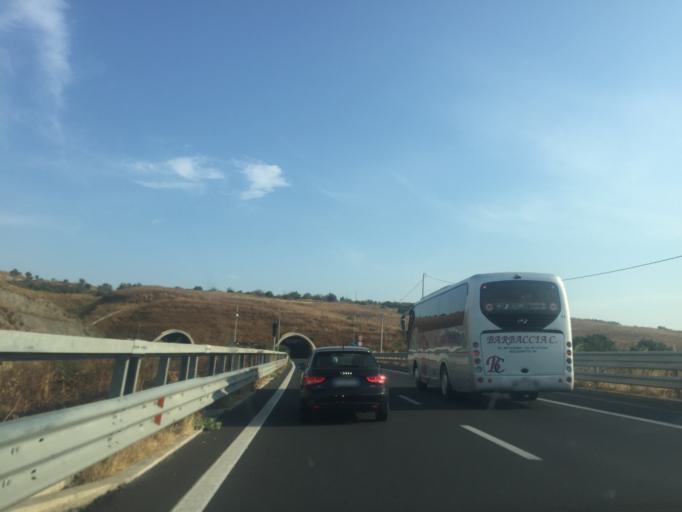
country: IT
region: Sicily
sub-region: Provincia di Siracusa
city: Lentini
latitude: 37.3589
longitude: 15.0476
